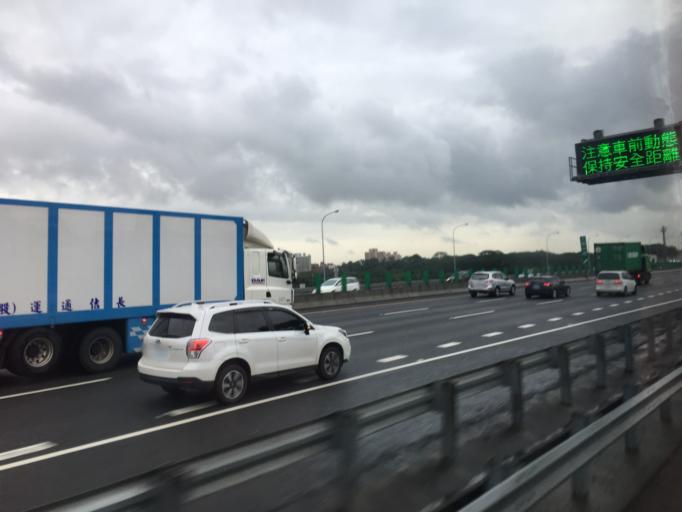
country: TW
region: Taiwan
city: Taoyuan City
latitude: 24.9822
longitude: 121.2310
